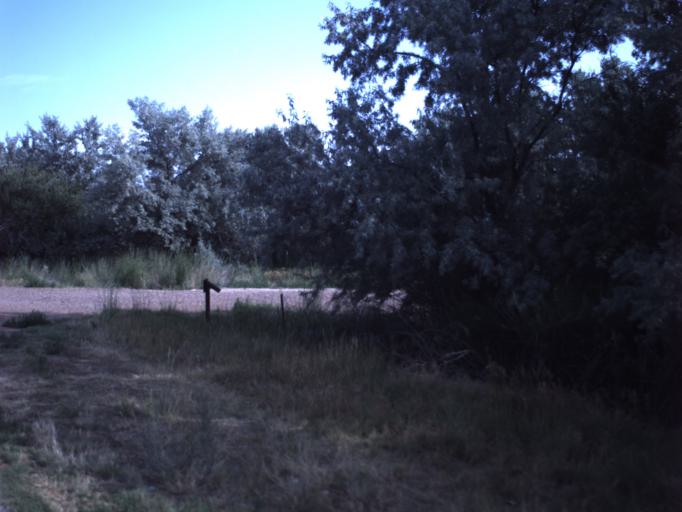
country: US
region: Utah
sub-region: Duchesne County
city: Duchesne
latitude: 40.3263
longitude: -110.2653
